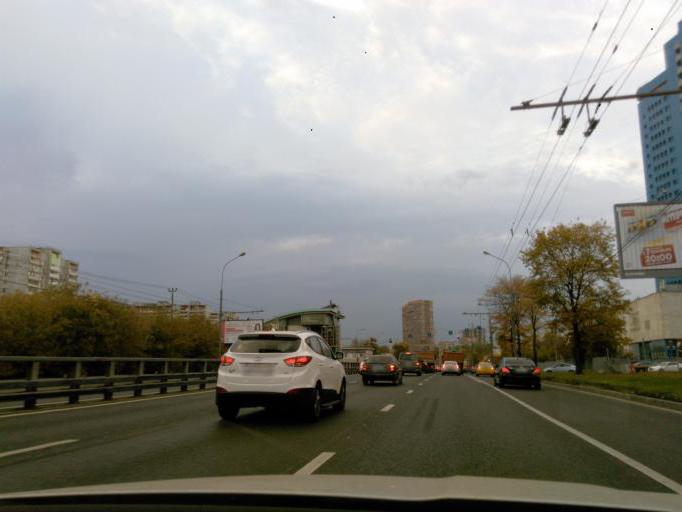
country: RU
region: Moscow
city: Likhobory
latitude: 55.8279
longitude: 37.5727
